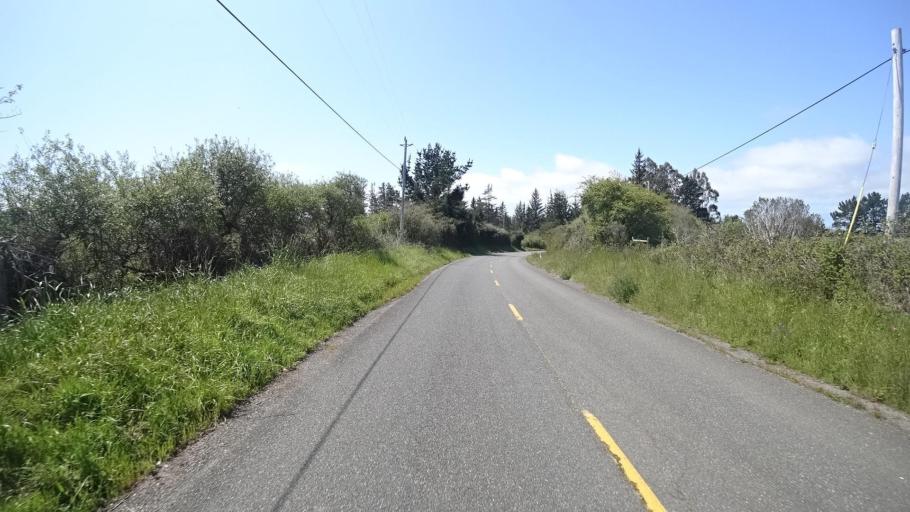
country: US
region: California
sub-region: Humboldt County
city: Fortuna
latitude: 40.6421
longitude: -124.2060
